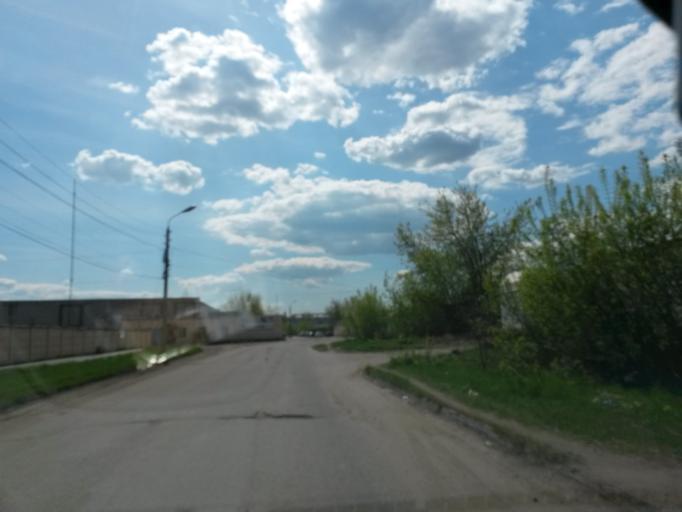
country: RU
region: Jaroslavl
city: Yaroslavl
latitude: 57.6168
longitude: 39.8533
